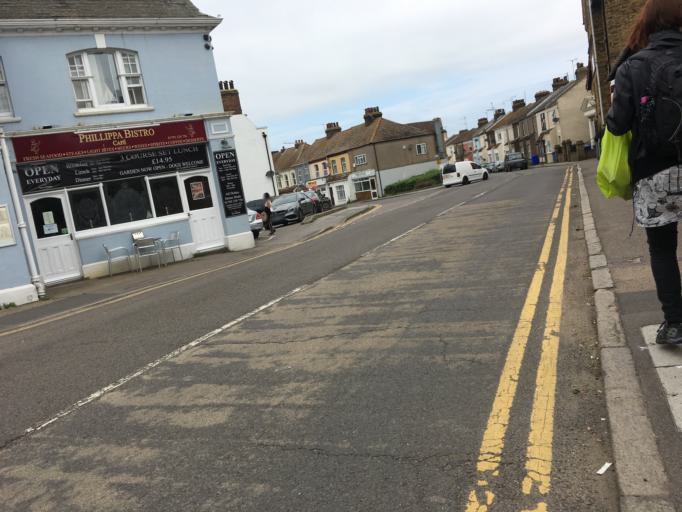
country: GB
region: England
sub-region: Kent
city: Queenborough
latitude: 51.4162
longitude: 0.7477
